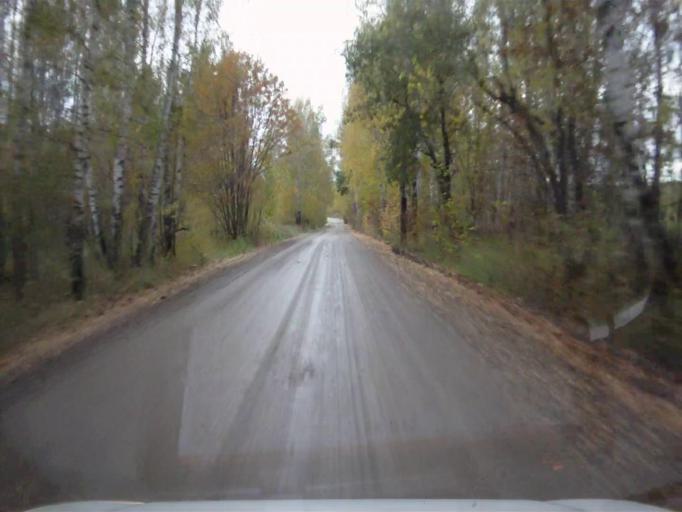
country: RU
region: Sverdlovsk
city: Mikhaylovsk
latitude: 56.1726
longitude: 59.2194
